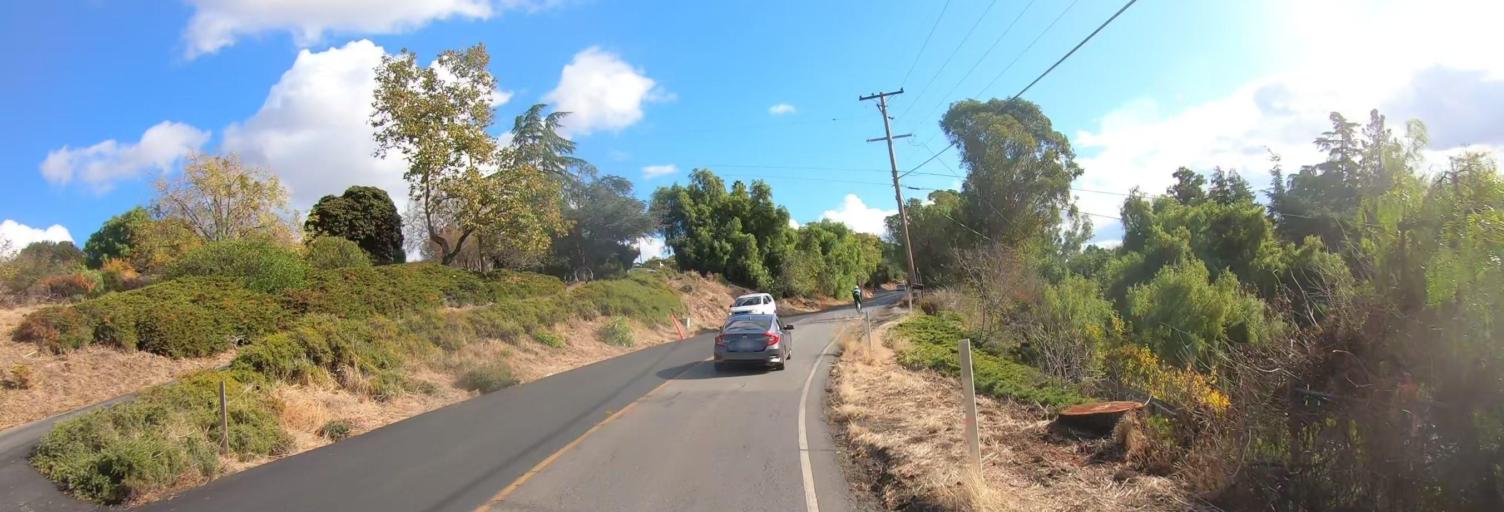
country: US
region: California
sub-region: Santa Clara County
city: East Foothills
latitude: 37.3820
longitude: -121.8131
